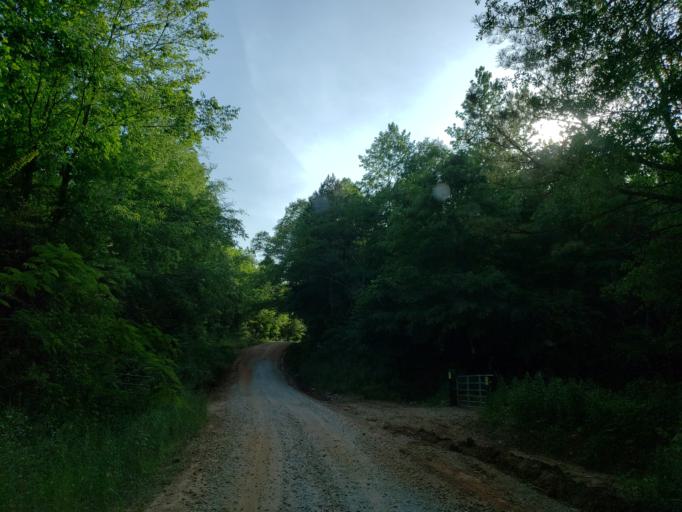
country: US
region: Georgia
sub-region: Carroll County
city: Bowdon
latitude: 33.4764
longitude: -85.3081
